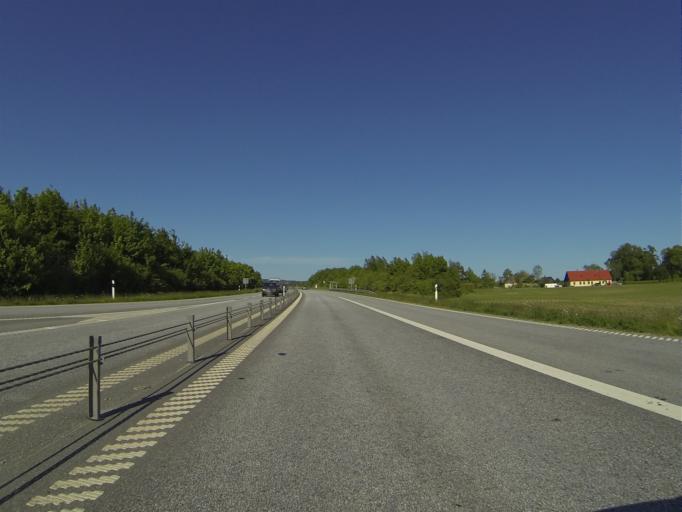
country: SE
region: Skane
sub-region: Svedala Kommun
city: Klagerup
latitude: 55.6444
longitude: 13.2697
